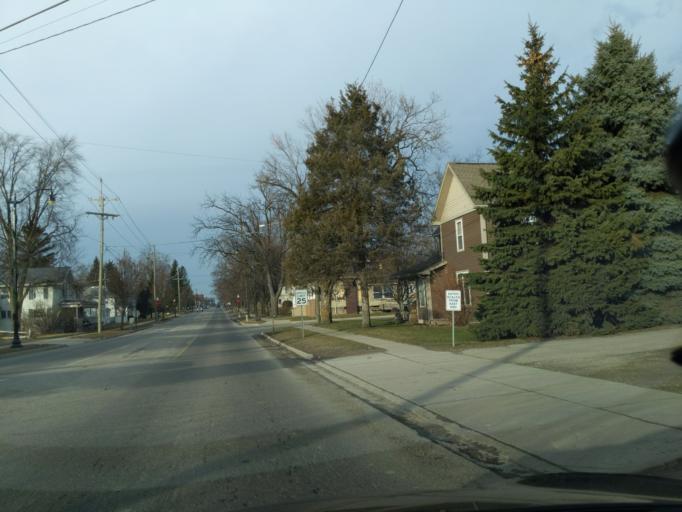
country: US
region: Michigan
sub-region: Livingston County
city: Fowlerville
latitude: 42.6559
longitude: -84.0729
